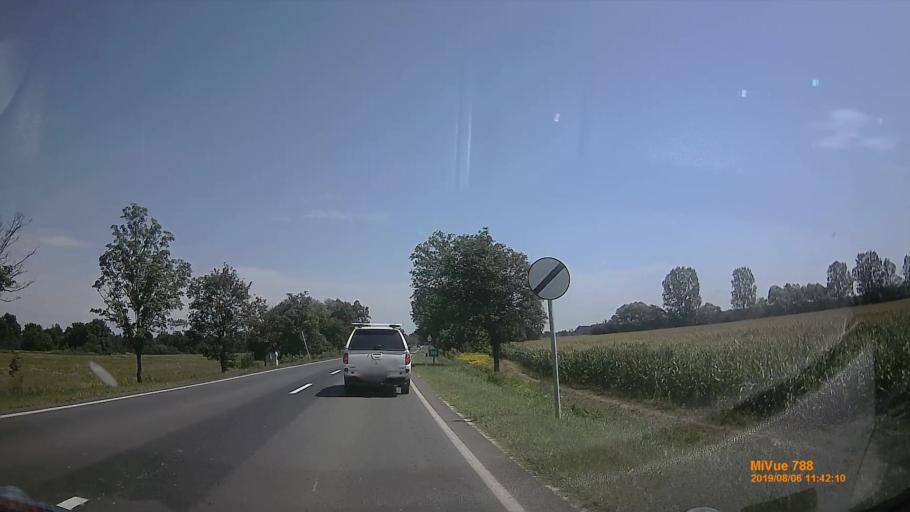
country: HU
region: Vas
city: Kormend
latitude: 46.9961
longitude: 16.5390
